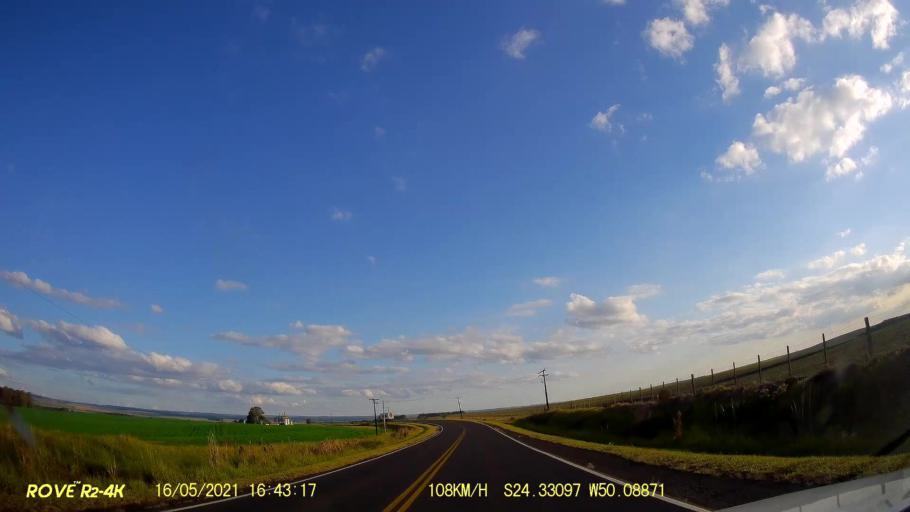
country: BR
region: Parana
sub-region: Pirai Do Sul
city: Pirai do Sul
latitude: -24.3315
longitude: -50.0888
